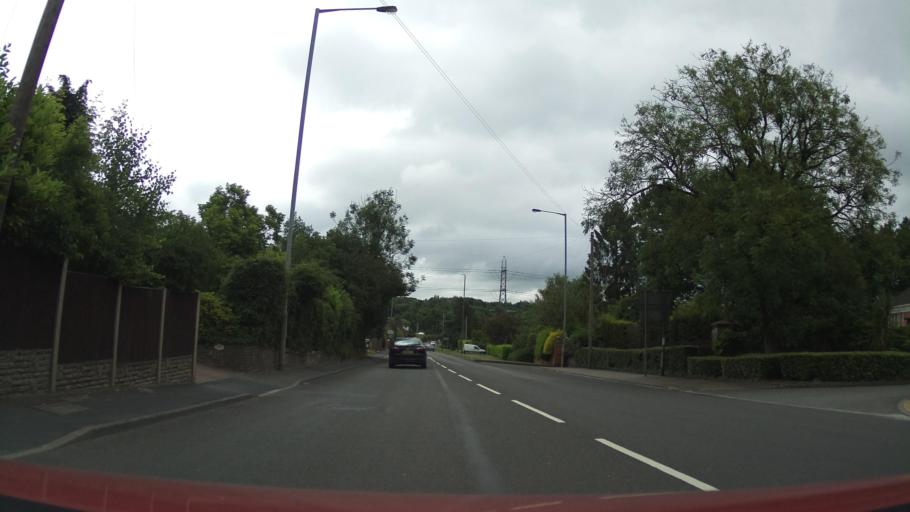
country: GB
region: England
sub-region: Derbyshire
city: Swadlincote
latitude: 52.8001
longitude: -1.5898
